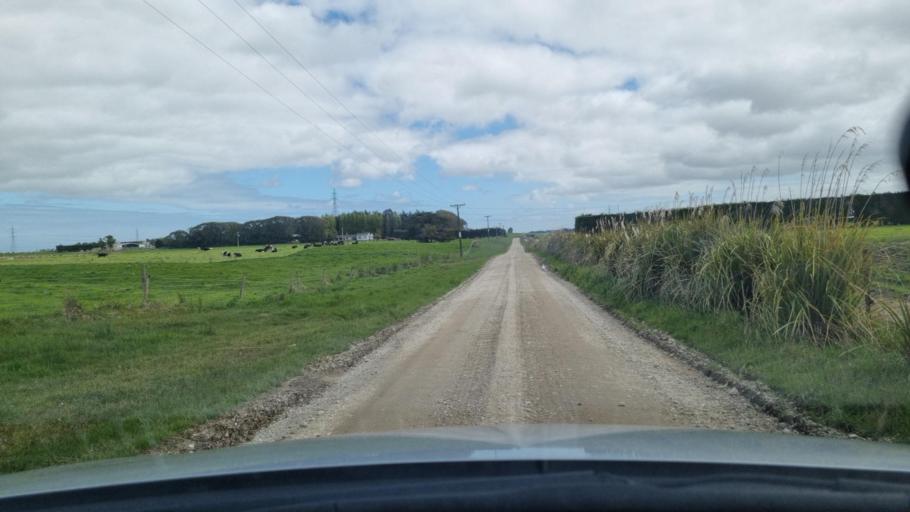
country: NZ
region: Southland
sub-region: Invercargill City
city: Invercargill
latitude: -46.4558
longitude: 168.4554
